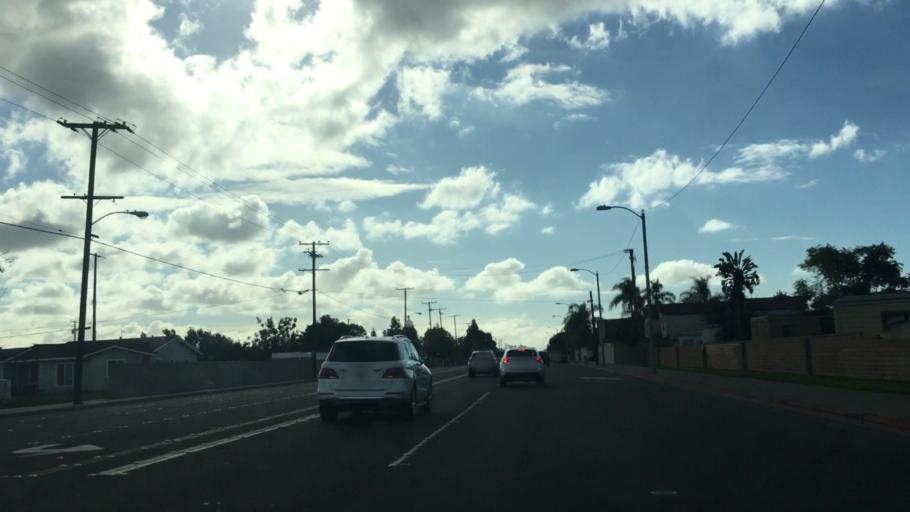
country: US
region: California
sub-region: Orange County
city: Midway City
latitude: 33.7575
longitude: -117.9725
